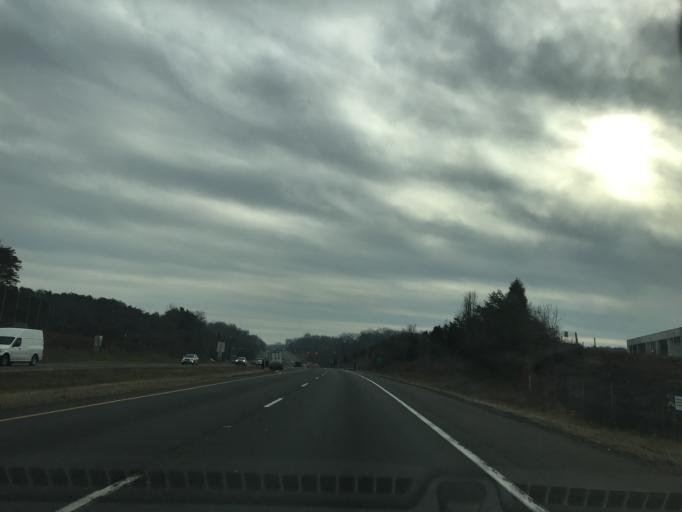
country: US
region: Virginia
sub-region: City of Manassas
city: Manassas
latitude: 38.7246
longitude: -77.4989
